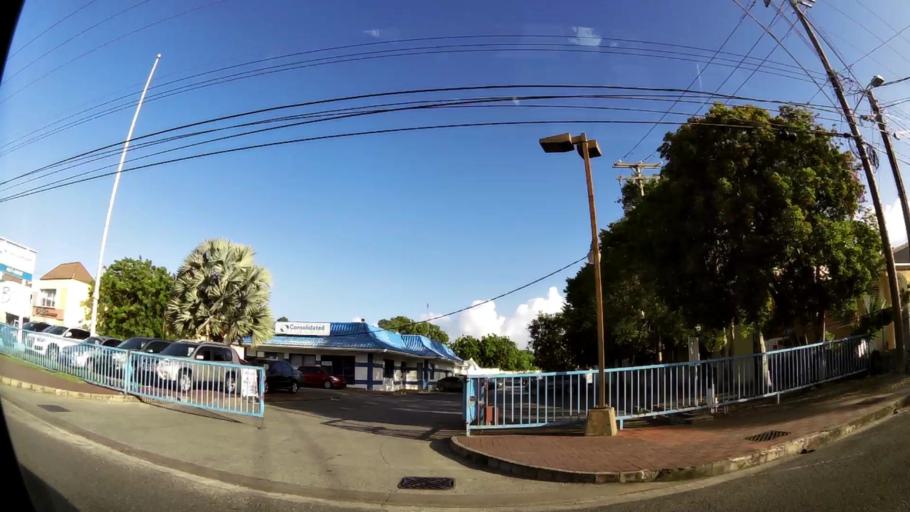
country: BB
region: Saint Michael
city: Bridgetown
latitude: 13.0742
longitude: -59.5926
